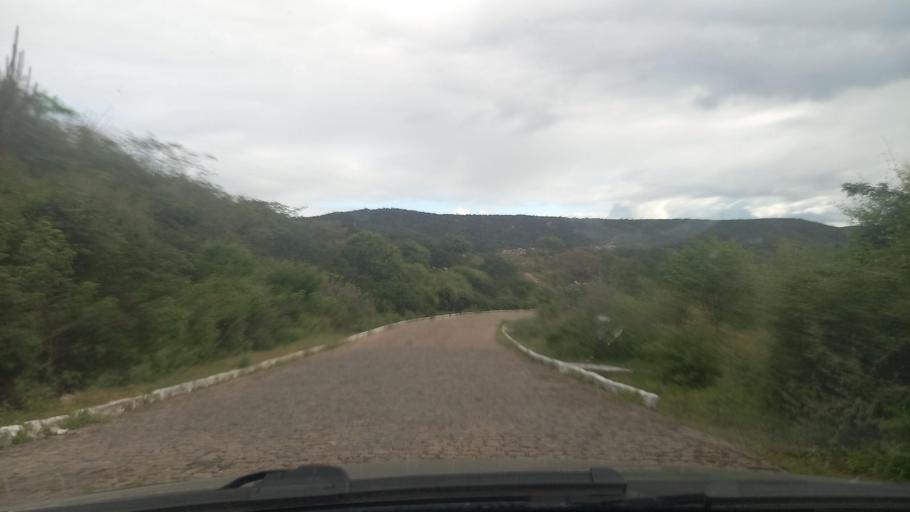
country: BR
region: Sergipe
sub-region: Caninde De Sao Francisco
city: Caninde de Sao Francisco
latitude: -9.6235
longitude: -37.8052
